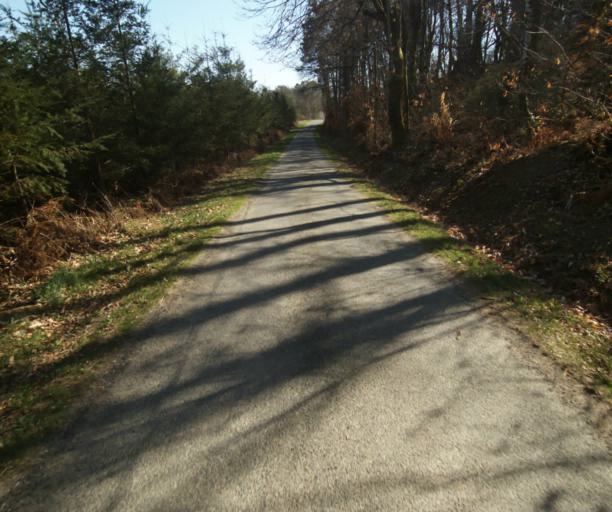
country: FR
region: Limousin
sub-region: Departement de la Correze
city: Saint-Mexant
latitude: 45.2899
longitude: 1.6414
